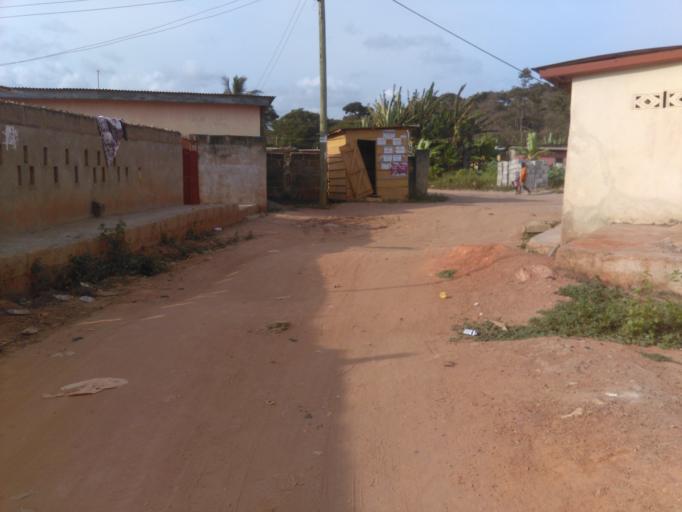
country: GH
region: Central
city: Cape Coast
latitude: 5.1134
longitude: -1.2966
